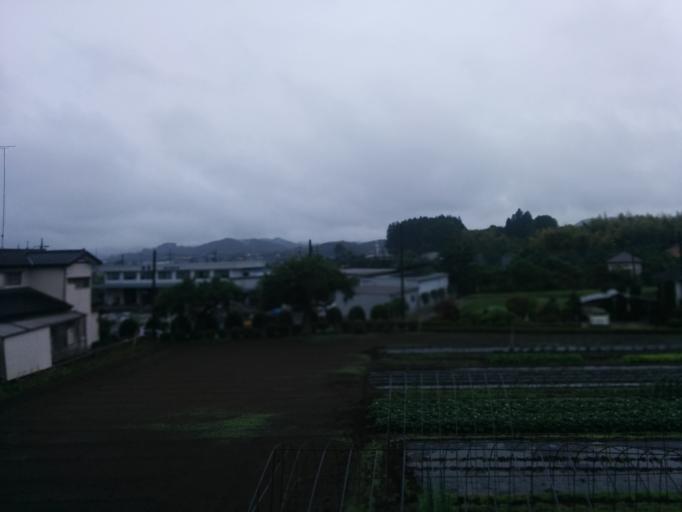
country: JP
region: Tochigi
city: Kanuma
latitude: 36.5752
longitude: 139.7607
